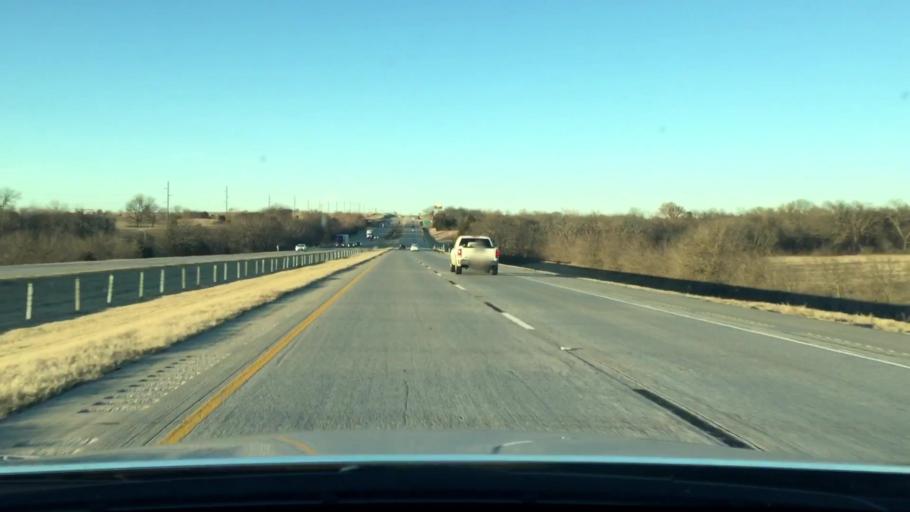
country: US
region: Oklahoma
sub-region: Love County
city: Marietta
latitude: 33.8746
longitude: -97.1340
